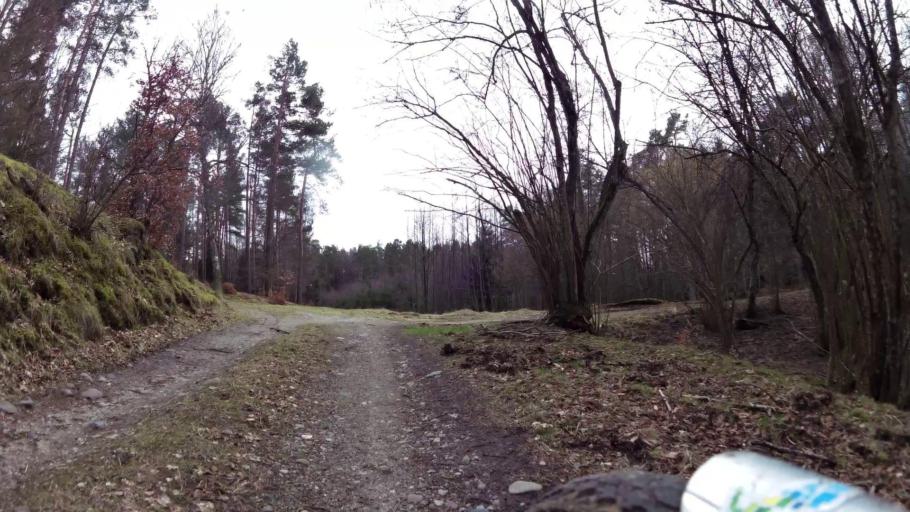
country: PL
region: Pomeranian Voivodeship
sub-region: Powiat bytowski
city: Trzebielino
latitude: 54.1480
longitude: 17.1583
